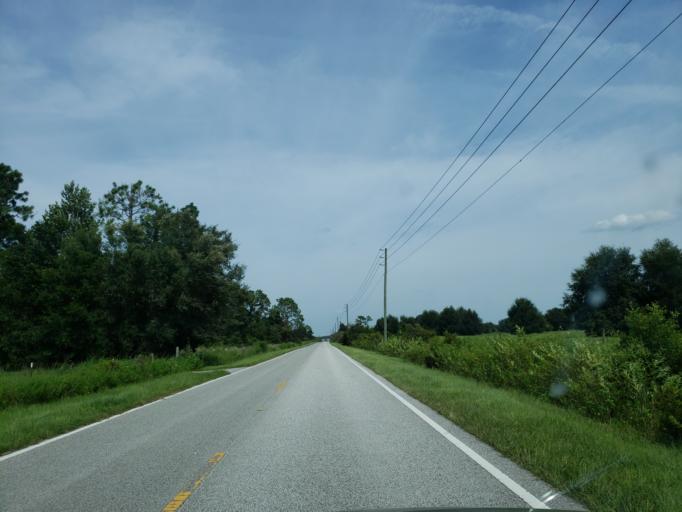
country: US
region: Florida
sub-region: Pasco County
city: Wesley Chapel
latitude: 28.2794
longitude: -82.3015
